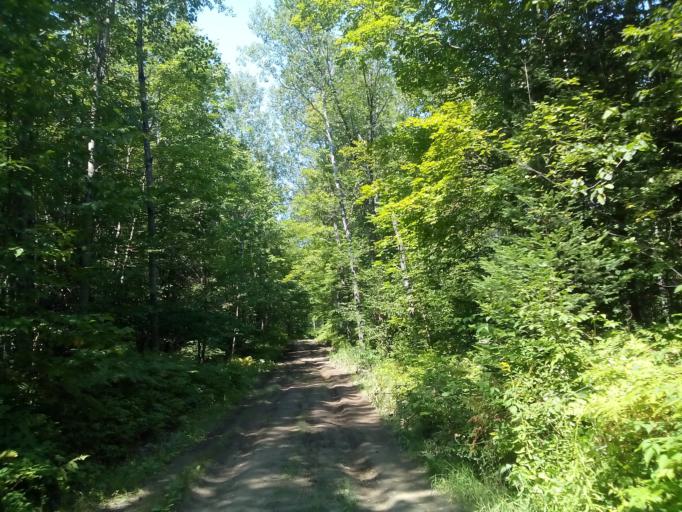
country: US
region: Wisconsin
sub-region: Forest County
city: Crandon
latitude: 45.3644
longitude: -88.5214
